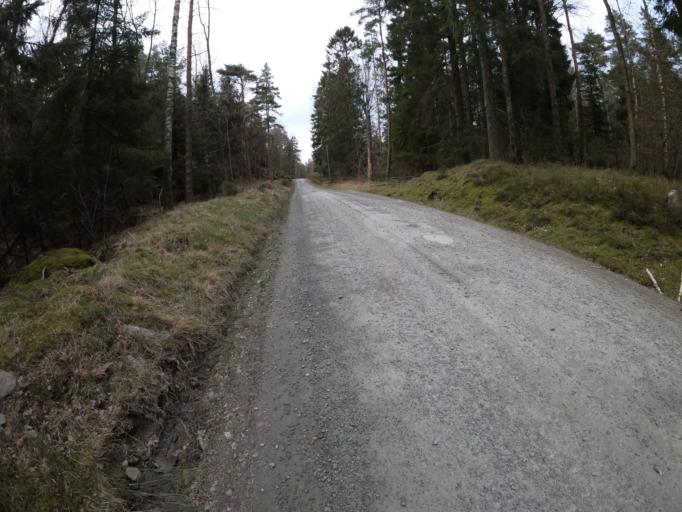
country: SE
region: Vaestra Goetaland
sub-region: Harryda Kommun
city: Molnlycke
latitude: 57.6369
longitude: 12.1008
